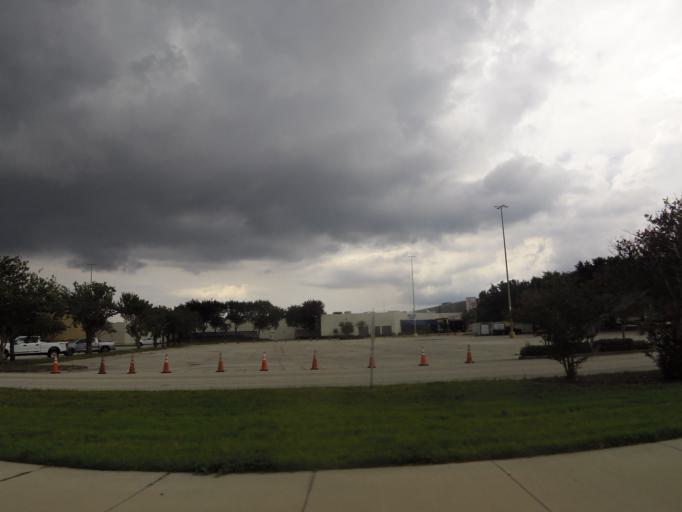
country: US
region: Florida
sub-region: Duval County
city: Jacksonville
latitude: 30.3219
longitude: -81.5534
